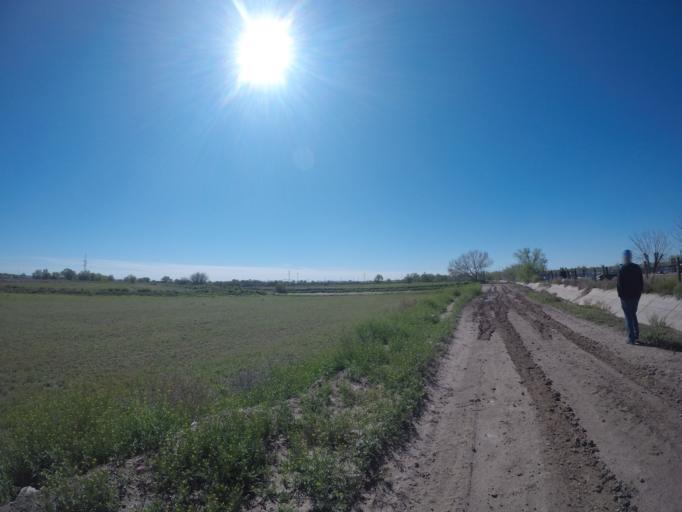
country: US
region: Texas
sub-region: El Paso County
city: Socorro
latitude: 31.6401
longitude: -106.3349
